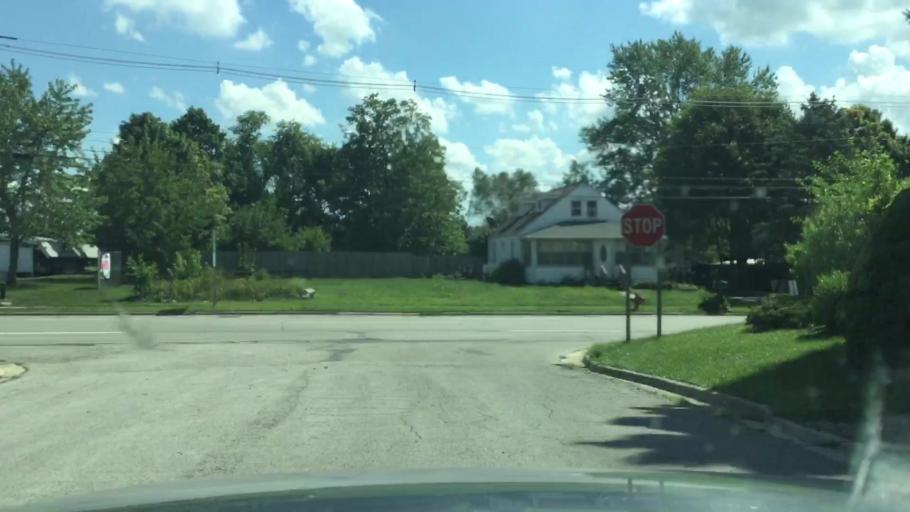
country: US
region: Michigan
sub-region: Lenawee County
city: Clinton
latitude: 42.0750
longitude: -83.9666
